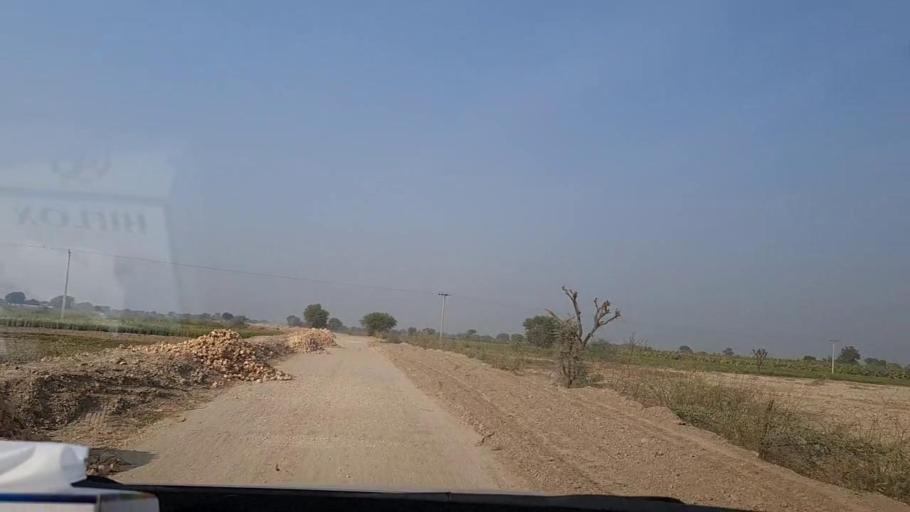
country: PK
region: Sindh
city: Tando Ghulam Ali
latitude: 25.1658
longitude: 68.8784
